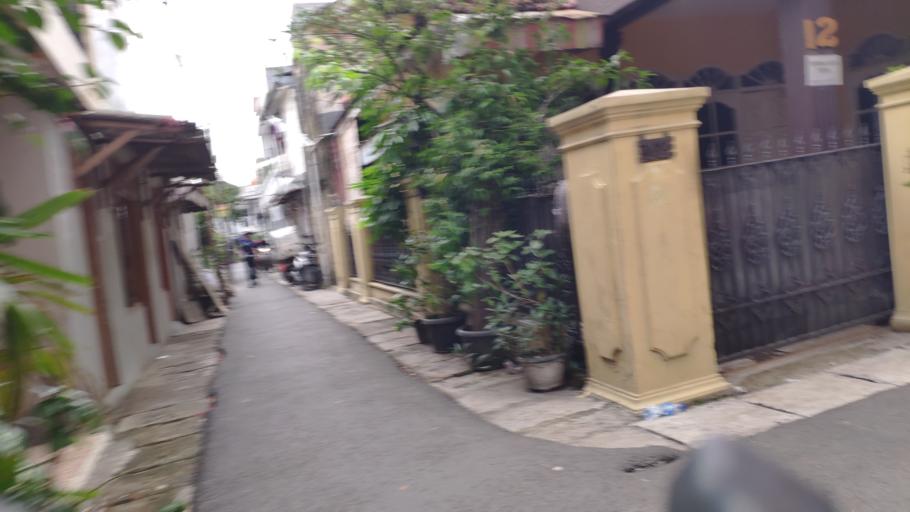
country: ID
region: Jakarta Raya
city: Jakarta
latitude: -6.2211
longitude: 106.8435
